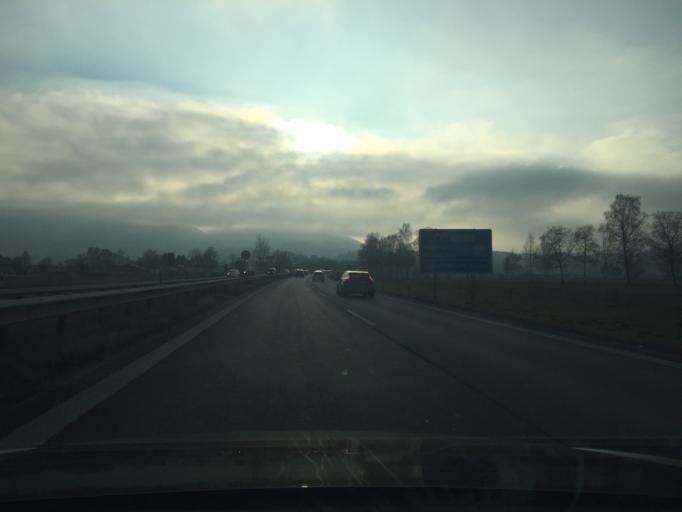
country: DE
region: Bavaria
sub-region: Upper Bavaria
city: Bernau am Chiemsee
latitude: 47.8252
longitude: 12.3829
